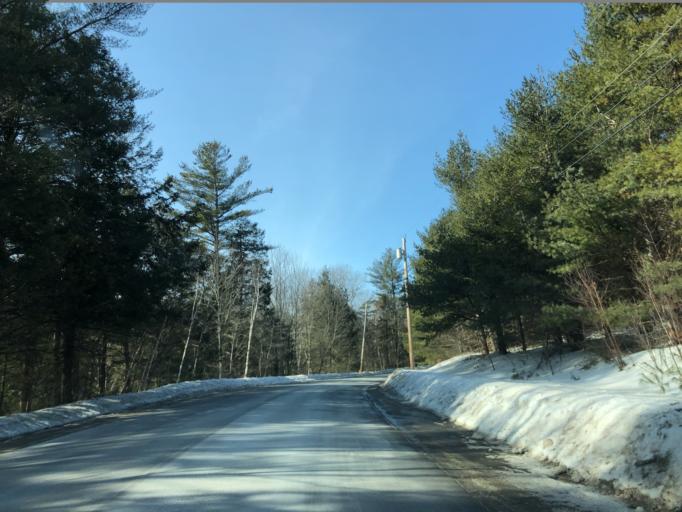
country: US
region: Maine
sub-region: Androscoggin County
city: Minot
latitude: 44.1433
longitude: -70.3259
